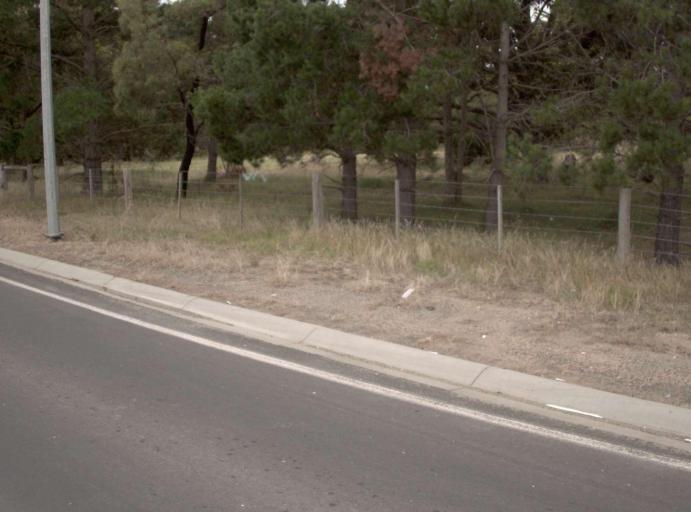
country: AU
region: Victoria
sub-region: Wellington
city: Sale
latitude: -38.0994
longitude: 146.9889
